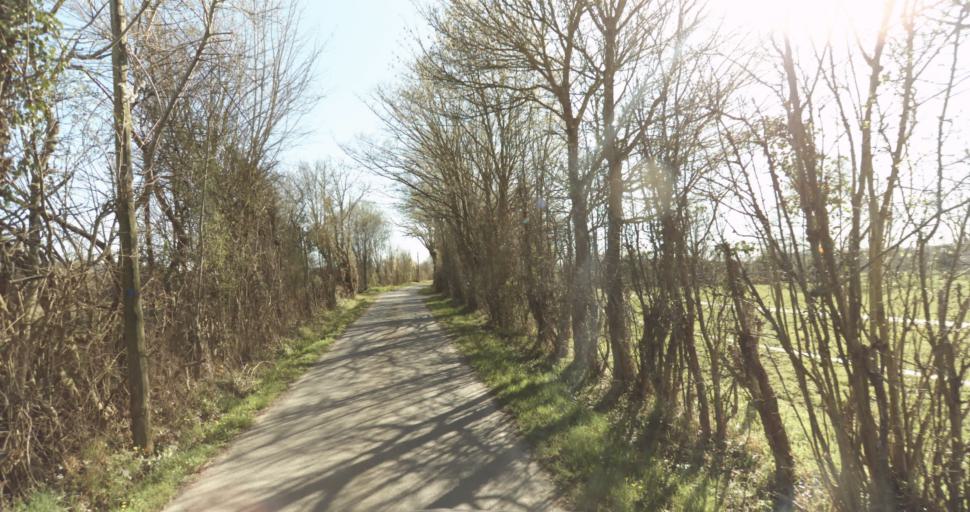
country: FR
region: Lower Normandy
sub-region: Departement du Calvados
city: Cambremer
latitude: 49.0561
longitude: 0.0599
